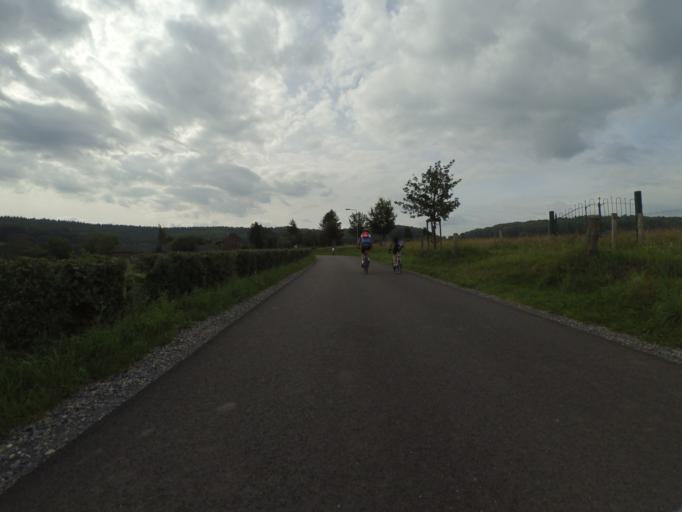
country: NL
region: Limburg
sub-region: Gemeente Vaals
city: Vaals
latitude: 50.7618
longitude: 6.0013
